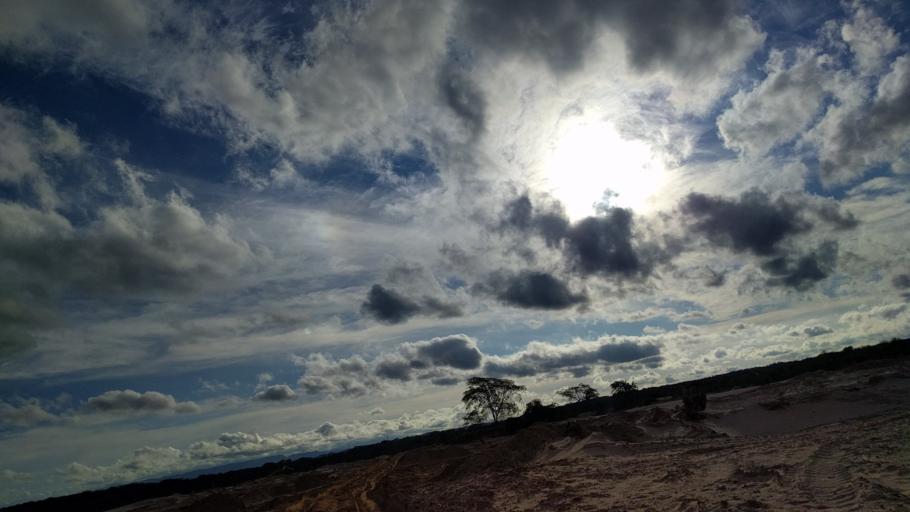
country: BO
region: Santa Cruz
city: Santa Cruz de la Sierra
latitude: -17.8533
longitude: -63.2812
